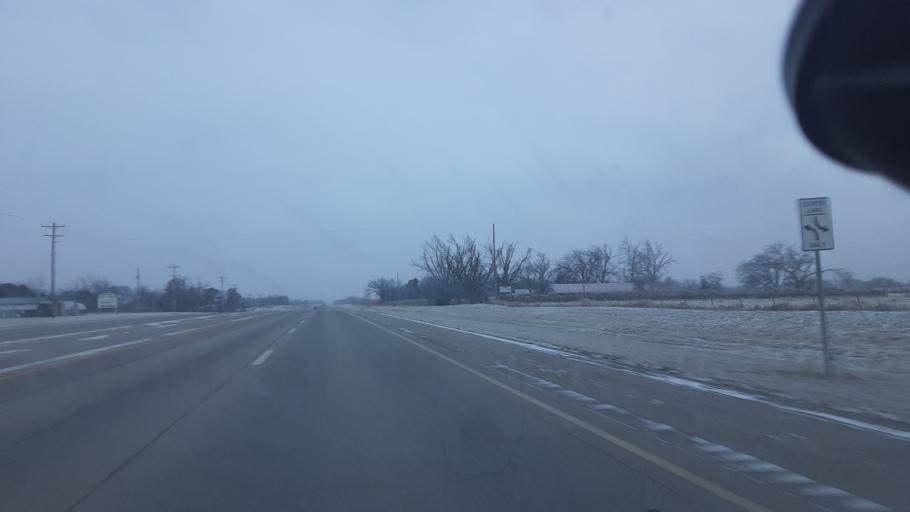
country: US
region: Oklahoma
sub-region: Payne County
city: Perkins
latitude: 35.9855
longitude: -97.0675
